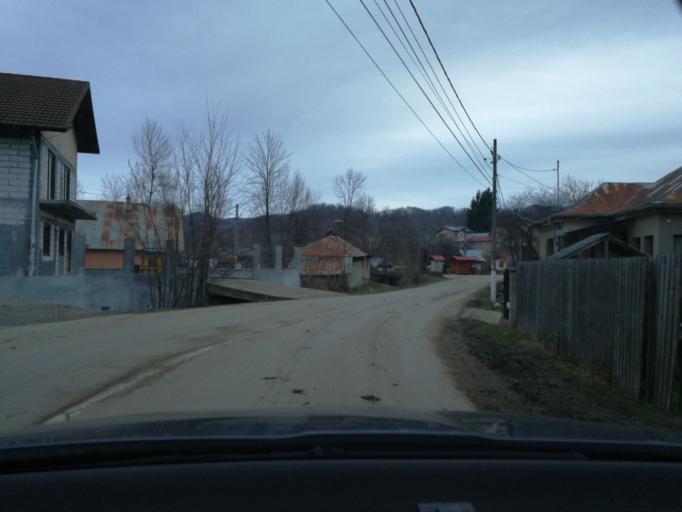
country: RO
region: Prahova
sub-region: Comuna Adunati
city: Ocina de Sus
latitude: 45.1830
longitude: 25.6067
